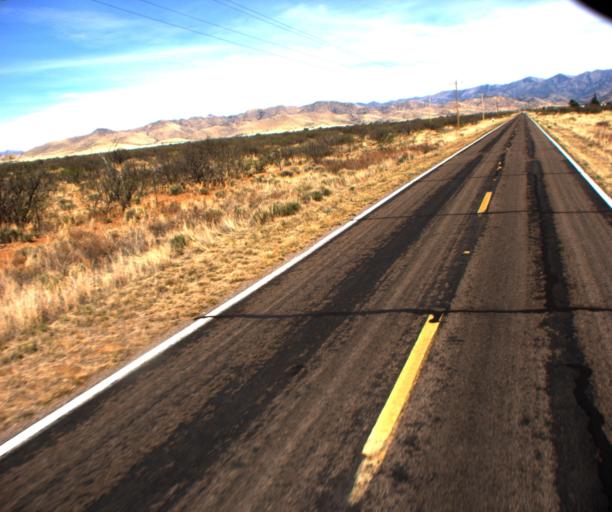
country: US
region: Arizona
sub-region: Cochise County
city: Willcox
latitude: 31.8760
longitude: -109.5082
